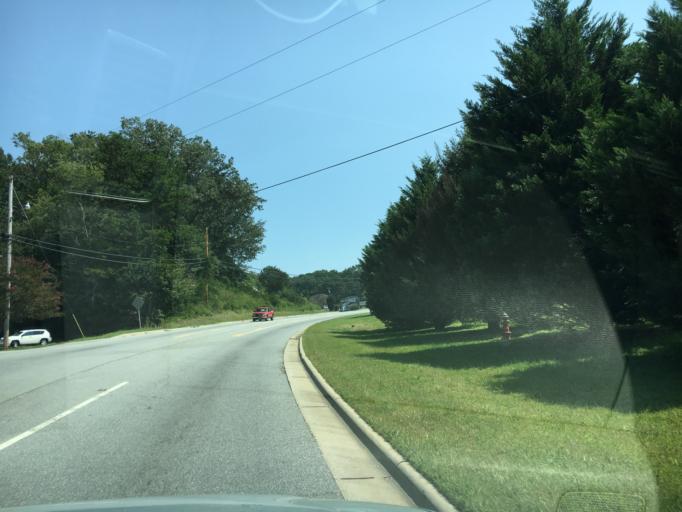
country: US
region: North Carolina
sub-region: McDowell County
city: Marion
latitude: 35.6609
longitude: -81.9680
